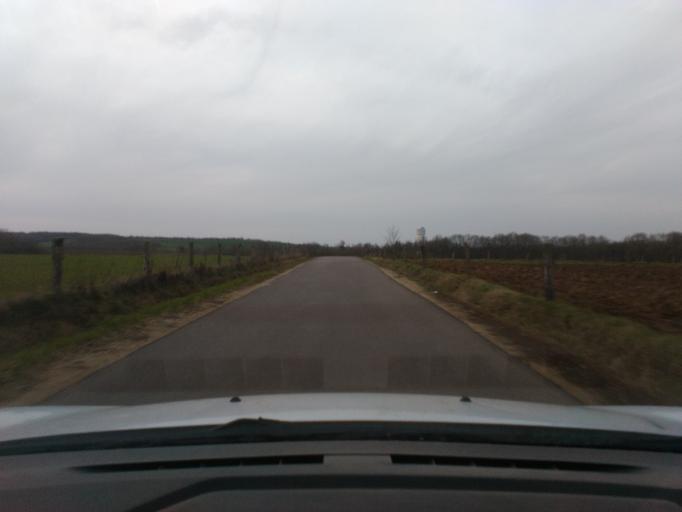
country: FR
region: Lorraine
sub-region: Departement des Vosges
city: Mirecourt
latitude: 48.2844
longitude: 6.1177
